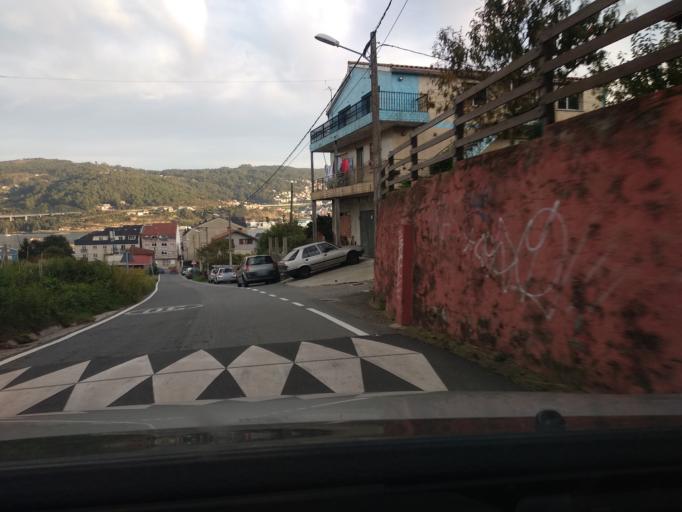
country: ES
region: Galicia
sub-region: Provincia de Pontevedra
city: Moana
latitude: 42.2870
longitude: -8.6850
